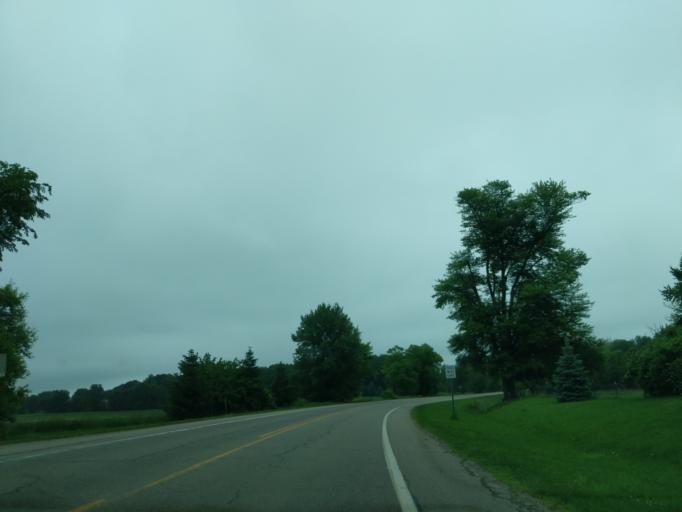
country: US
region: Michigan
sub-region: Hillsdale County
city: Litchfield
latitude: 42.0372
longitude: -84.7387
